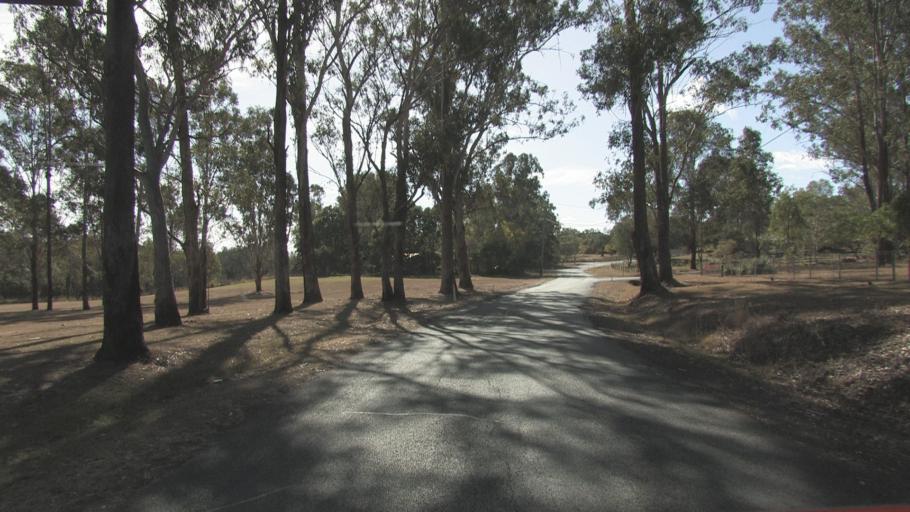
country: AU
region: Queensland
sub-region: Logan
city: Cedar Vale
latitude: -27.8584
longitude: 152.9801
